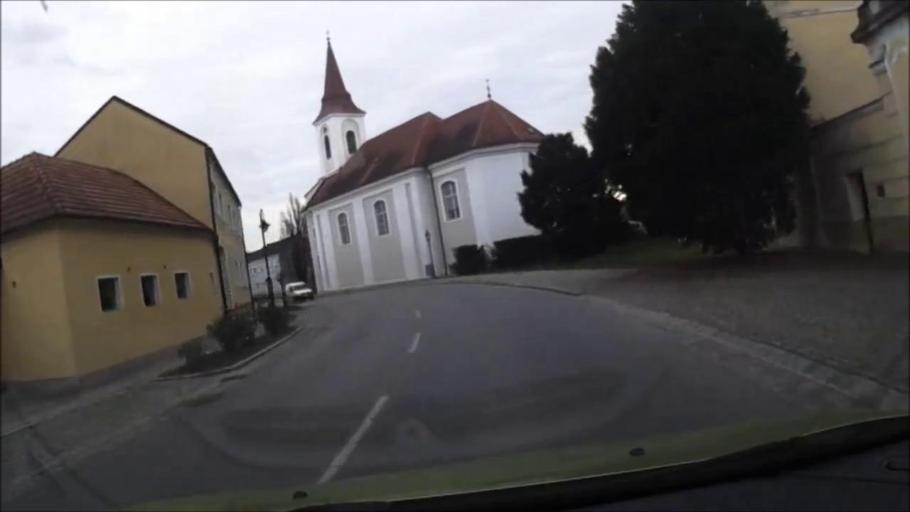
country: AT
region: Burgenland
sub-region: Eisenstadt-Umgebung
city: Leithaprodersdorf
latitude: 47.9391
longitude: 16.4718
